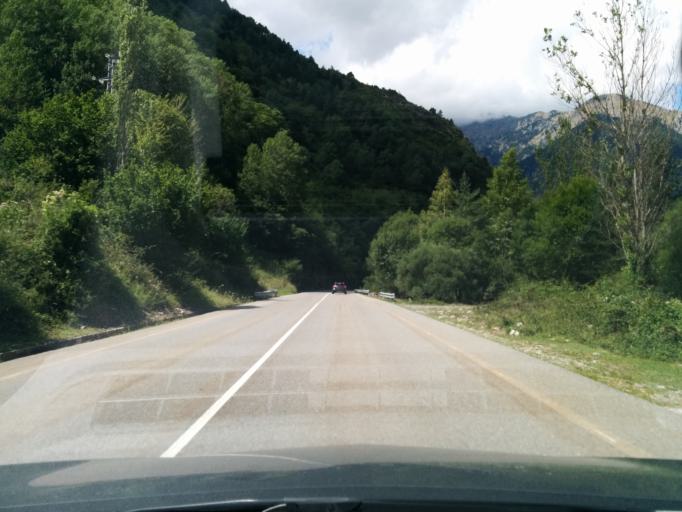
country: ES
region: Aragon
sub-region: Provincia de Huesca
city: Bielsa
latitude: 42.6469
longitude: 0.2109
